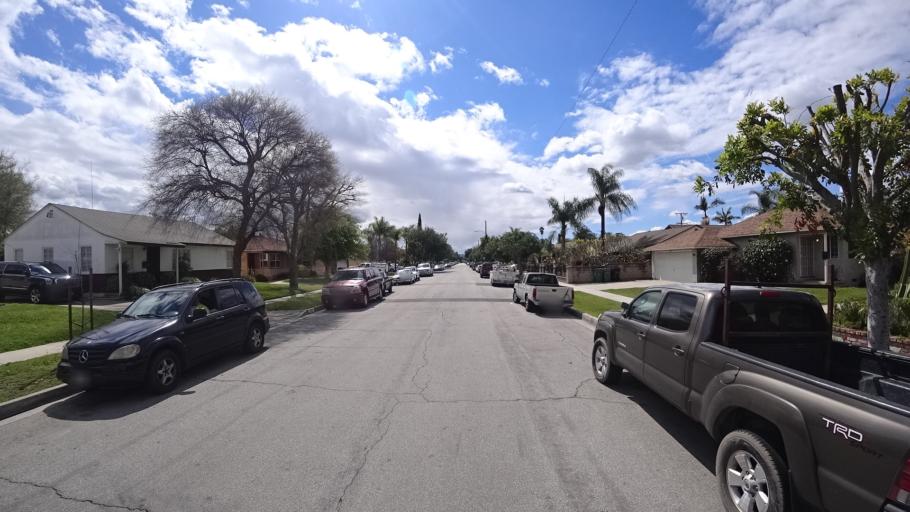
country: US
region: California
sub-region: Los Angeles County
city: Baldwin Park
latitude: 34.0900
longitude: -117.9703
